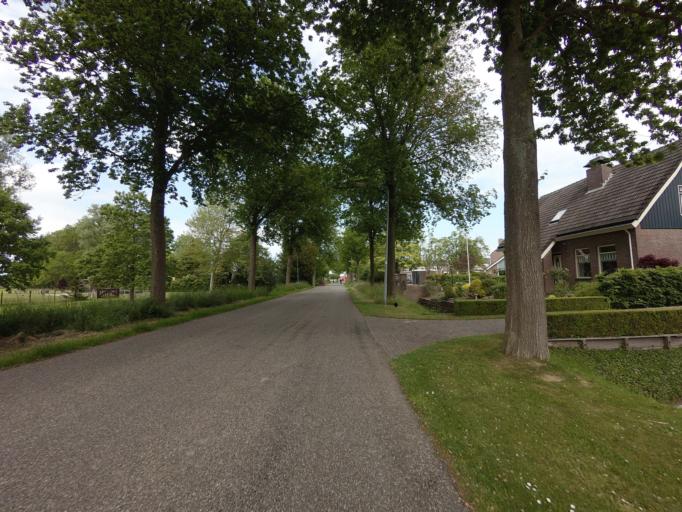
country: NL
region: North Holland
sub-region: Gemeente Hoorn
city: Hoorn
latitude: 52.6960
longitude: 5.0539
